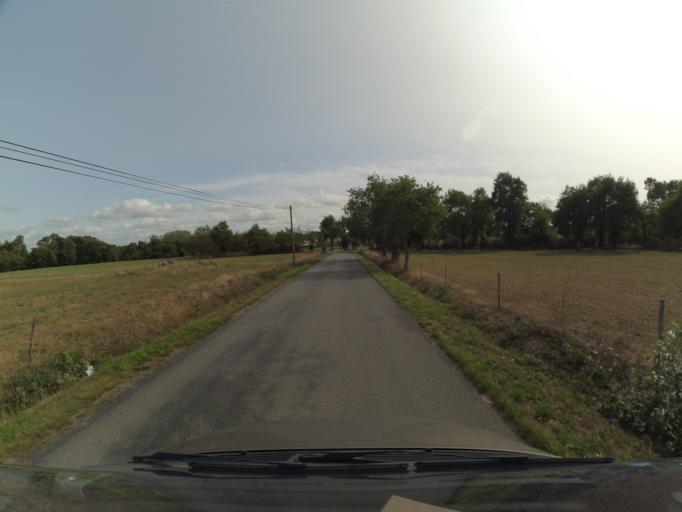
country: FR
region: Pays de la Loire
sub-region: Departement de la Vendee
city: La Bruffiere
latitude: 46.9995
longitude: -1.2008
